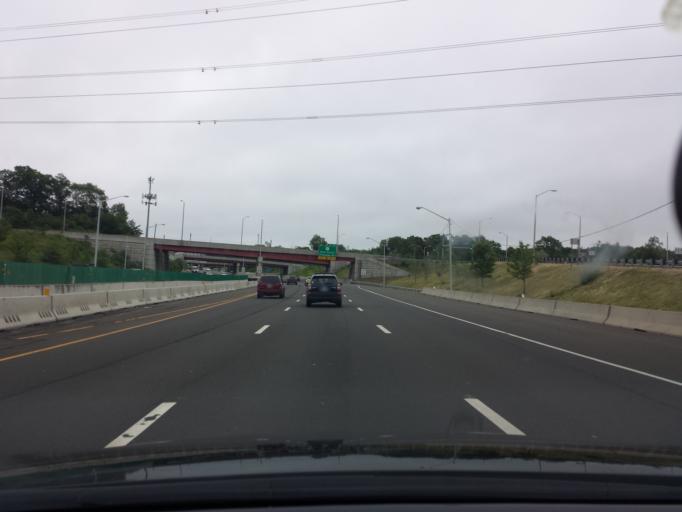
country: US
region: Connecticut
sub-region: New Haven County
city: East Haven
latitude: 41.2908
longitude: -72.8980
